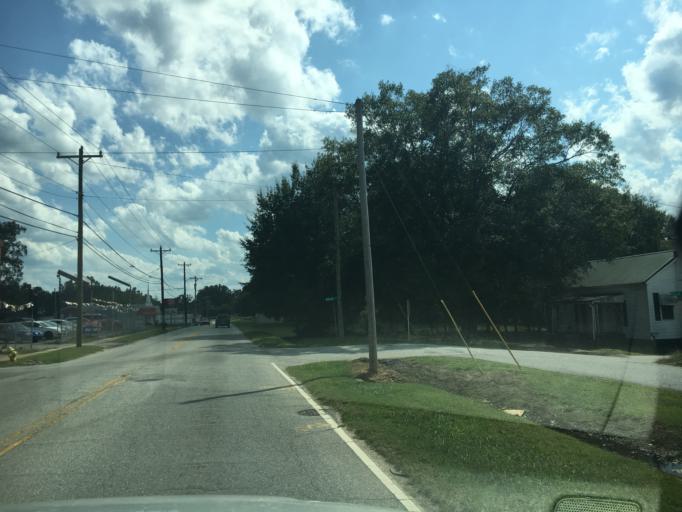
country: US
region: South Carolina
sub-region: Anderson County
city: Belton
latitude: 34.5303
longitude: -82.4957
